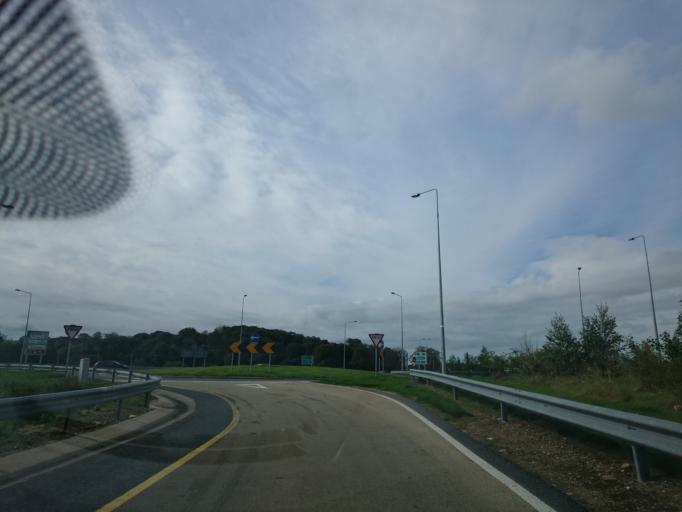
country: IE
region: Munster
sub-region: Waterford
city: Waterford
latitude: 52.2596
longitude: -7.1823
